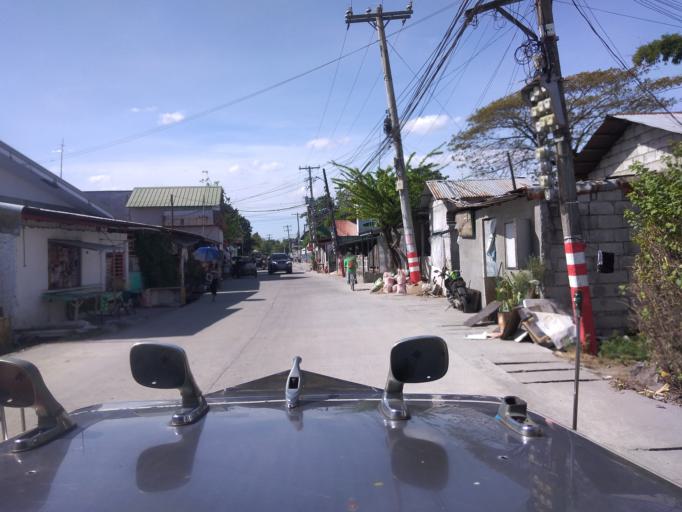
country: PH
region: Central Luzon
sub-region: Province of Pampanga
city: Magliman
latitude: 15.0345
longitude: 120.6654
